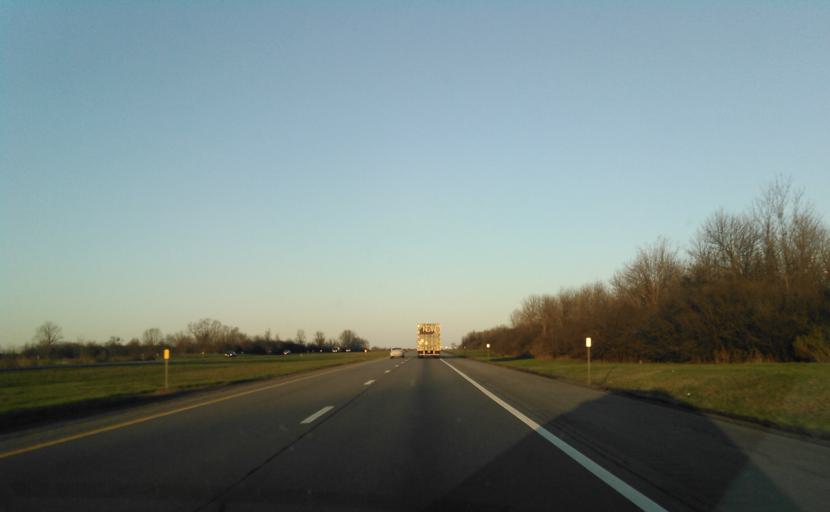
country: US
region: New York
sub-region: Ontario County
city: Clifton Springs
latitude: 42.9739
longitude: -77.1092
